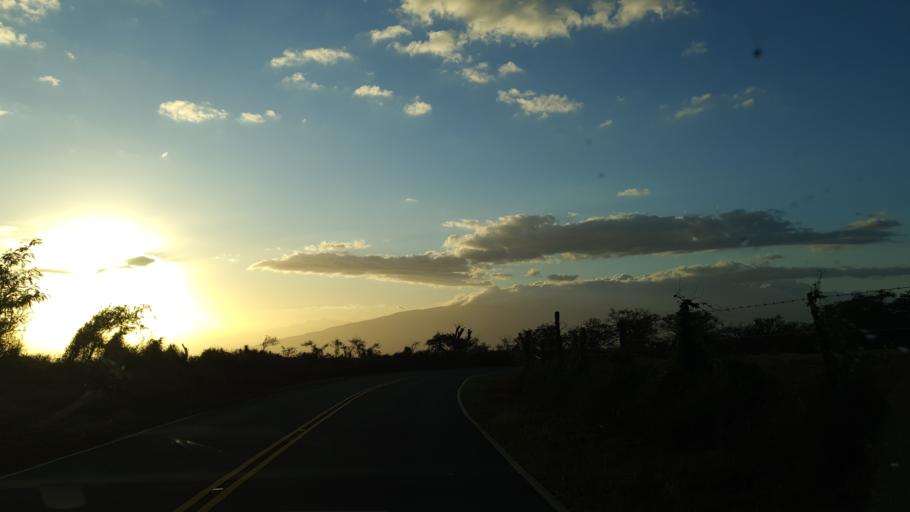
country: US
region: Hawaii
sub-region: Maui County
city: Pukalani
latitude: 20.7841
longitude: -156.3469
